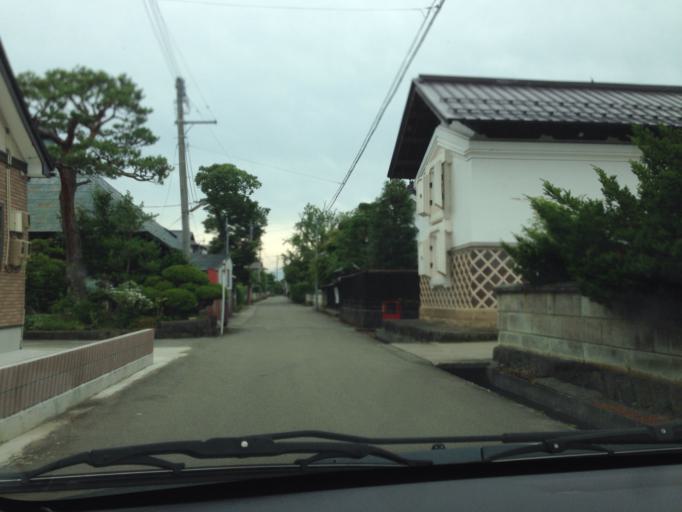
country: JP
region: Fukushima
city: Kitakata
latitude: 37.5624
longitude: 139.8702
